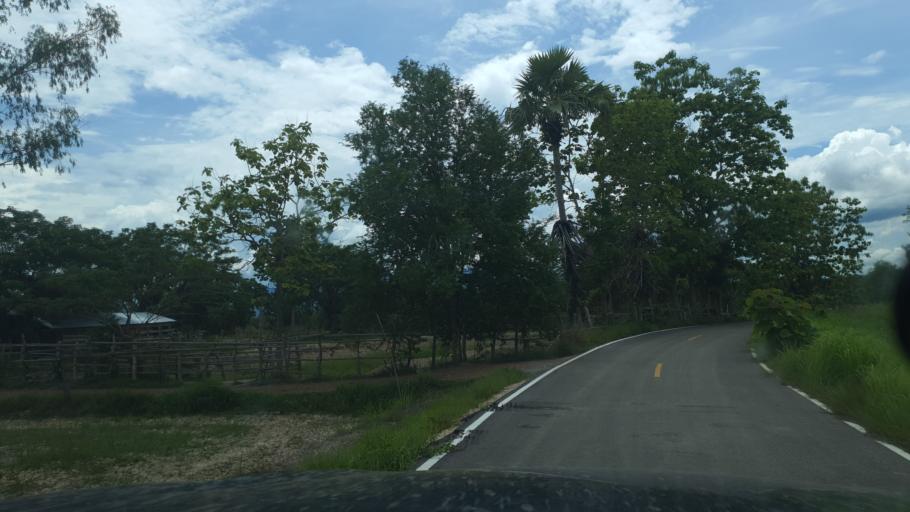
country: TH
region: Lampang
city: Sop Prap
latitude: 17.8649
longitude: 99.3918
